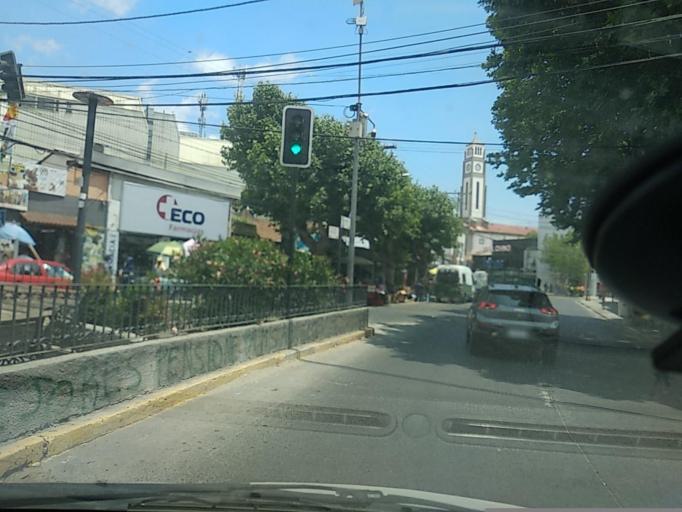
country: CL
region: Valparaiso
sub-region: Provincia de Marga Marga
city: Quilpue
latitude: -33.0461
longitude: -71.4404
